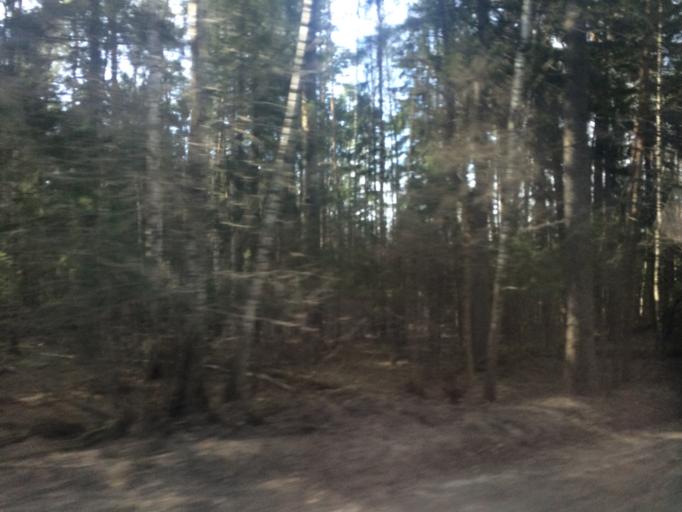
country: RU
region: Tatarstan
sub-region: Zelenodol'skiy Rayon
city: Vasil'yevo
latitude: 55.8948
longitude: 48.7287
